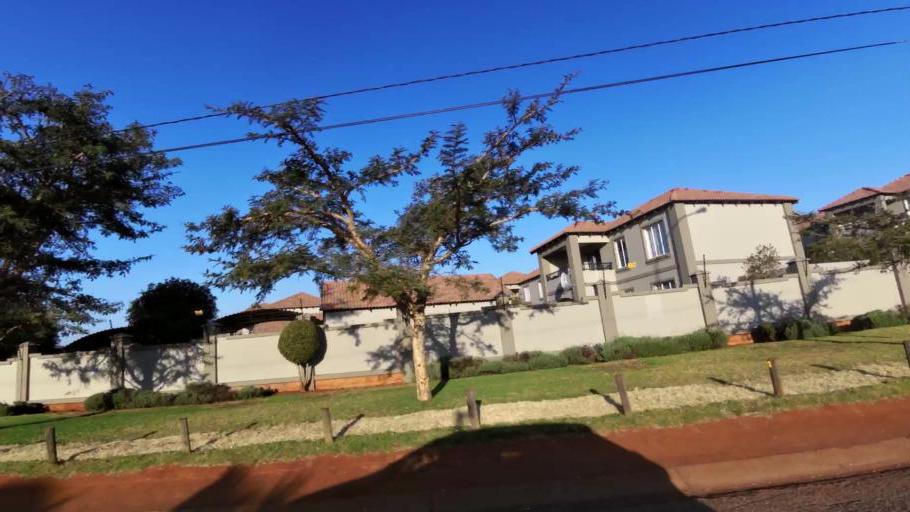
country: ZA
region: Gauteng
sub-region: City of Johannesburg Metropolitan Municipality
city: Roodepoort
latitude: -26.1694
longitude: 27.9457
